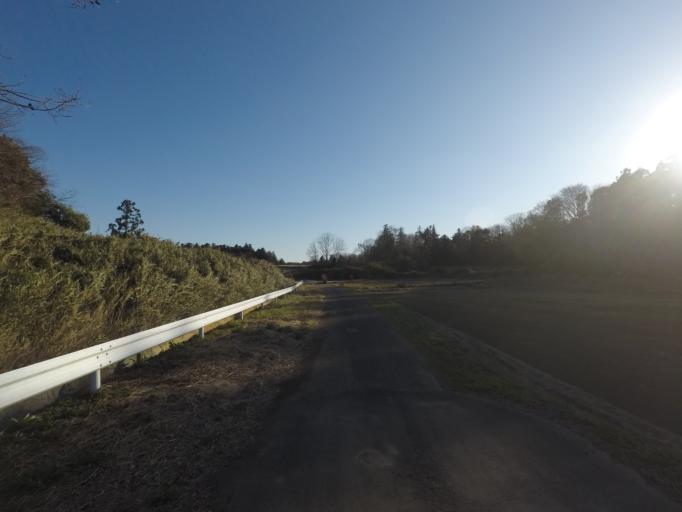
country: JP
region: Ibaraki
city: Ishige
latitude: 36.1349
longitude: 140.0039
